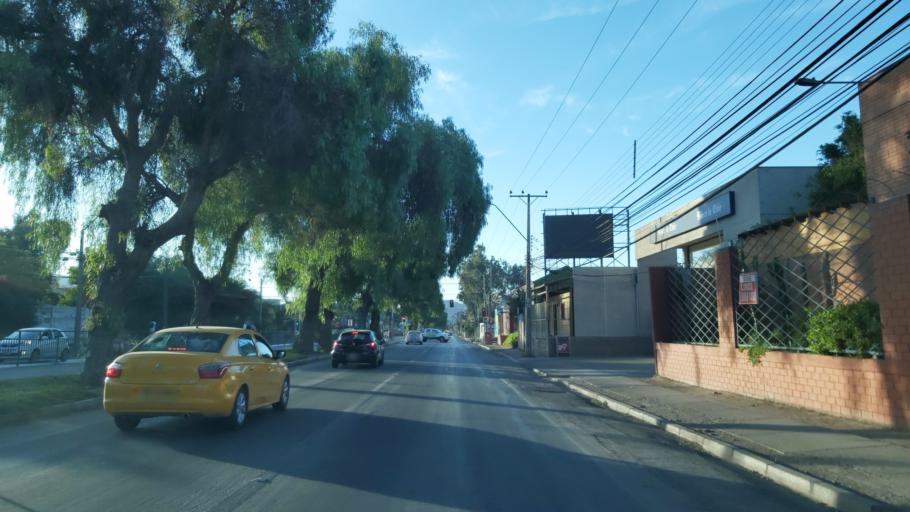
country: CL
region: Atacama
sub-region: Provincia de Copiapo
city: Copiapo
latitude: -27.3841
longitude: -70.3145
